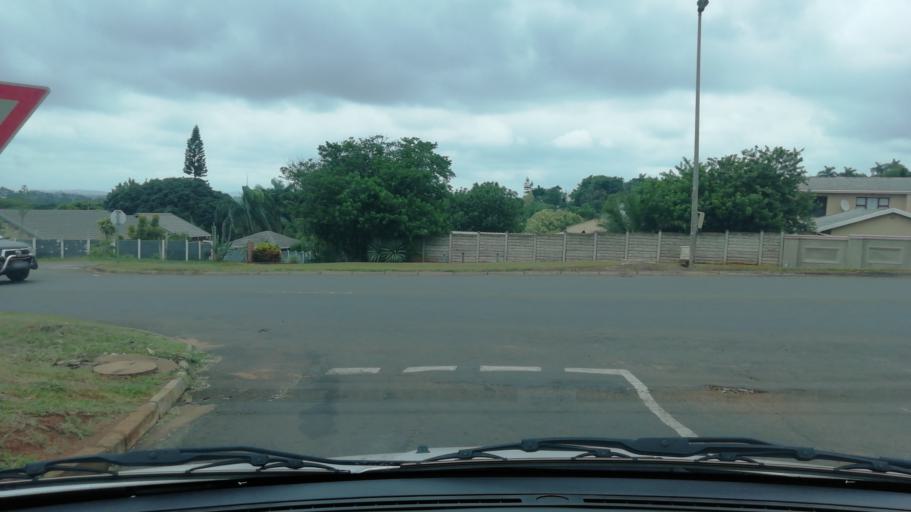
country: ZA
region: KwaZulu-Natal
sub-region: uThungulu District Municipality
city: Empangeni
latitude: -28.7694
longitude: 31.8951
